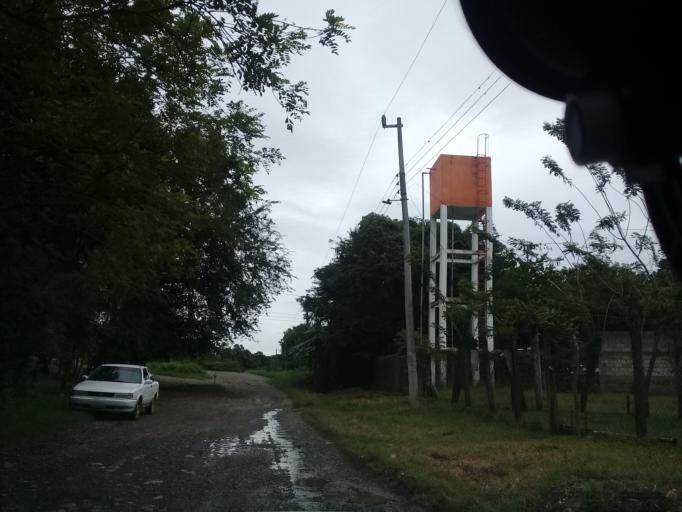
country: MX
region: Hidalgo
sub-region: Huejutla de Reyes
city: Chalahuiyapa
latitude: 21.1877
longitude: -98.3138
